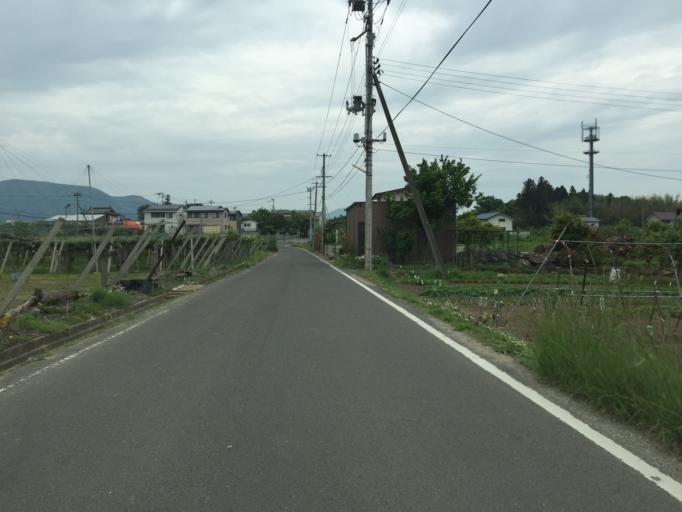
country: JP
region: Fukushima
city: Fukushima-shi
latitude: 37.7864
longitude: 140.4214
